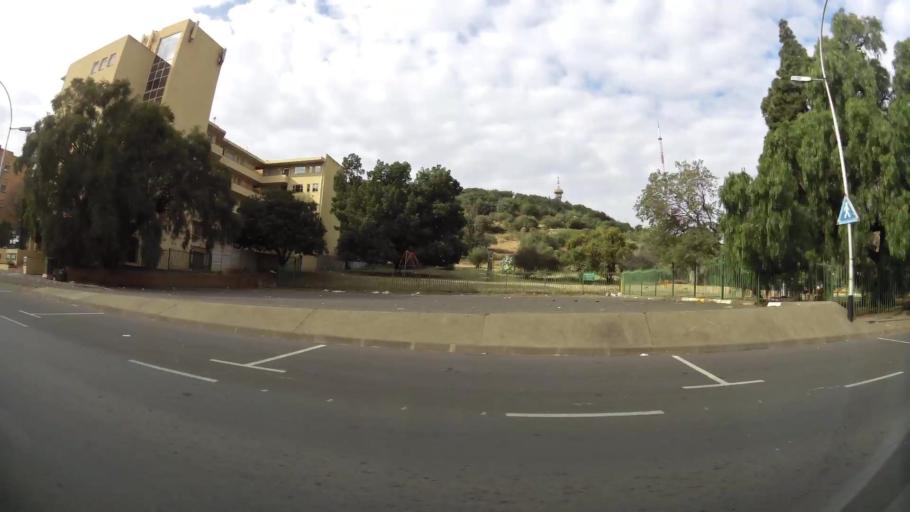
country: ZA
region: Orange Free State
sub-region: Mangaung Metropolitan Municipality
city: Bloemfontein
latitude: -29.1020
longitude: 26.2232
